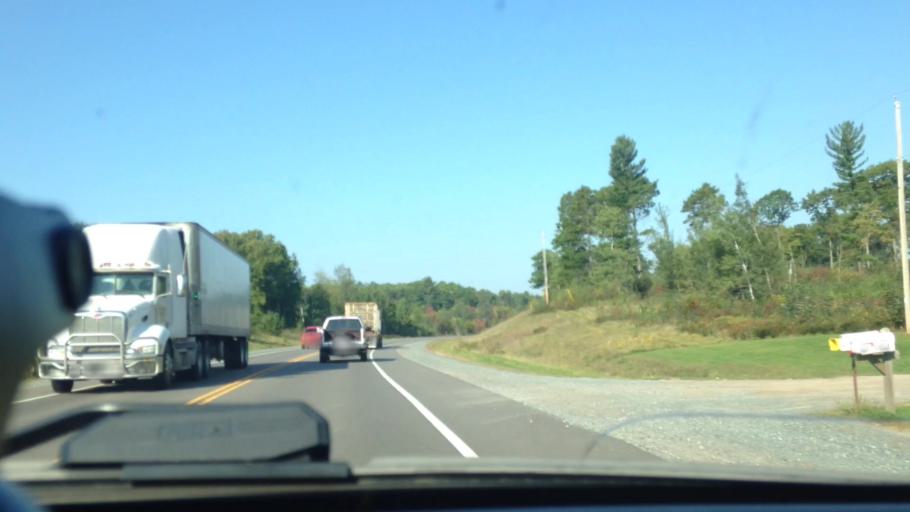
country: US
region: Michigan
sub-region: Dickinson County
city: Iron Mountain
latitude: 45.8760
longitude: -88.1118
